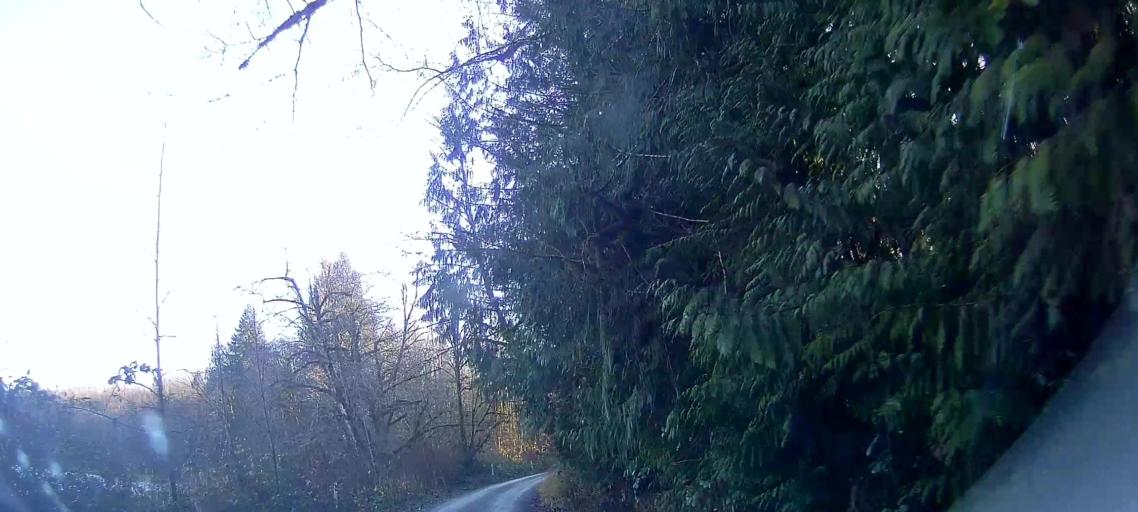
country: US
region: Washington
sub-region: Snohomish County
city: Darrington
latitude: 48.5437
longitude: -121.7272
